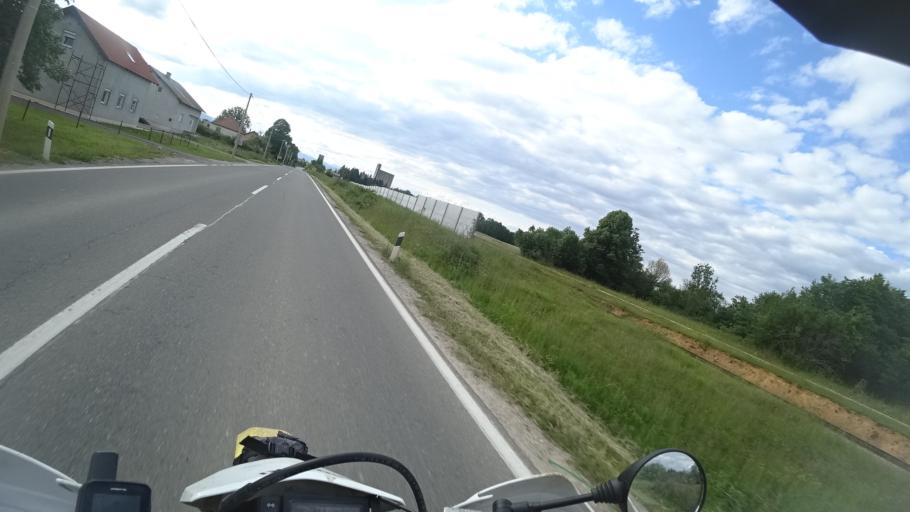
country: HR
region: Licko-Senjska
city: Gospic
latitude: 44.5296
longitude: 15.4042
